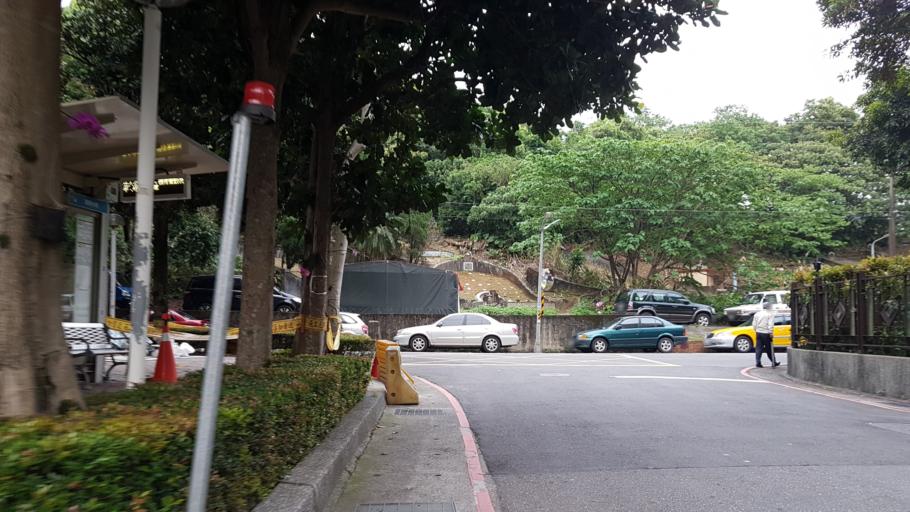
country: TW
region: Taipei
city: Taipei
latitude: 25.0046
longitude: 121.5485
